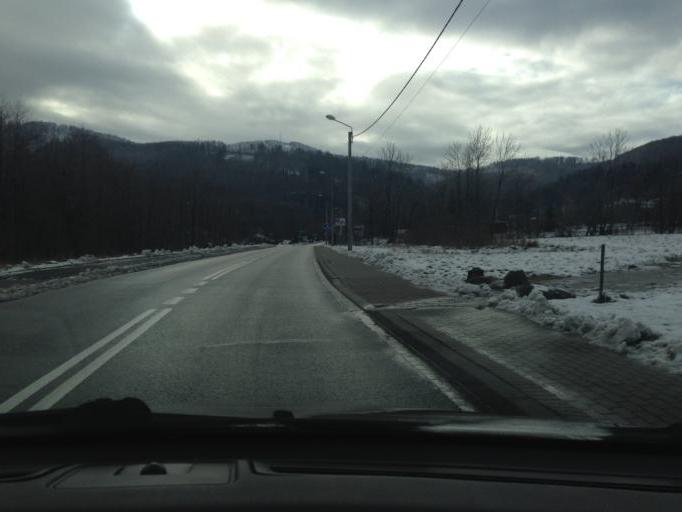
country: PL
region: Silesian Voivodeship
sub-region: Powiat bielski
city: Bystra
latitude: 49.7820
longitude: 19.0260
